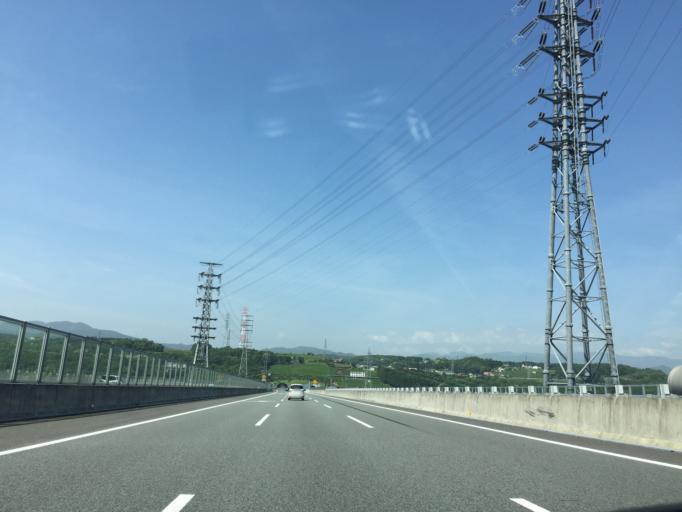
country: JP
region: Shizuoka
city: Fujinomiya
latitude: 35.1988
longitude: 138.6457
